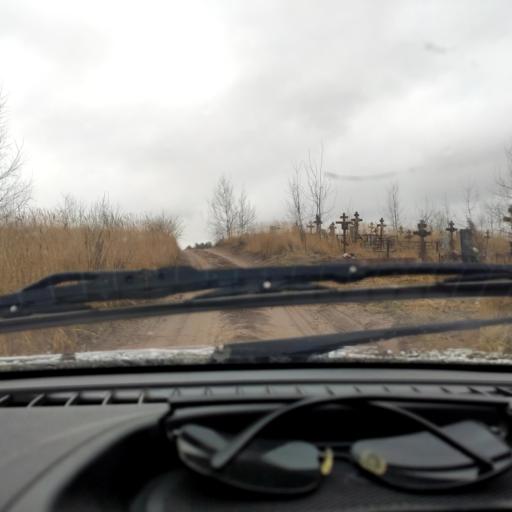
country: RU
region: Samara
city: Zhigulevsk
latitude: 53.5406
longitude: 49.5530
